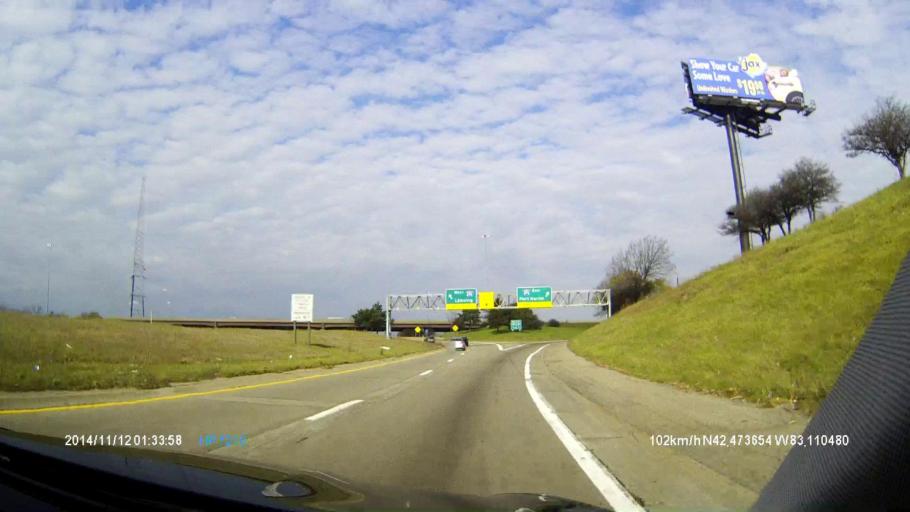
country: US
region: Michigan
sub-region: Oakland County
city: Hazel Park
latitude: 42.4735
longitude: -83.1105
